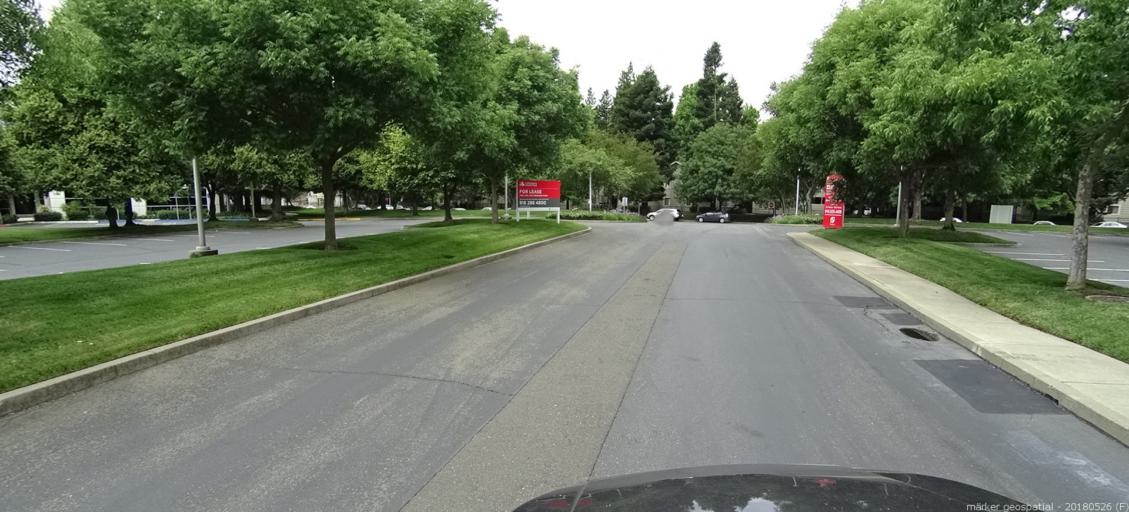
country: US
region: California
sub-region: Sacramento County
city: Sacramento
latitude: 38.6093
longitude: -121.5014
